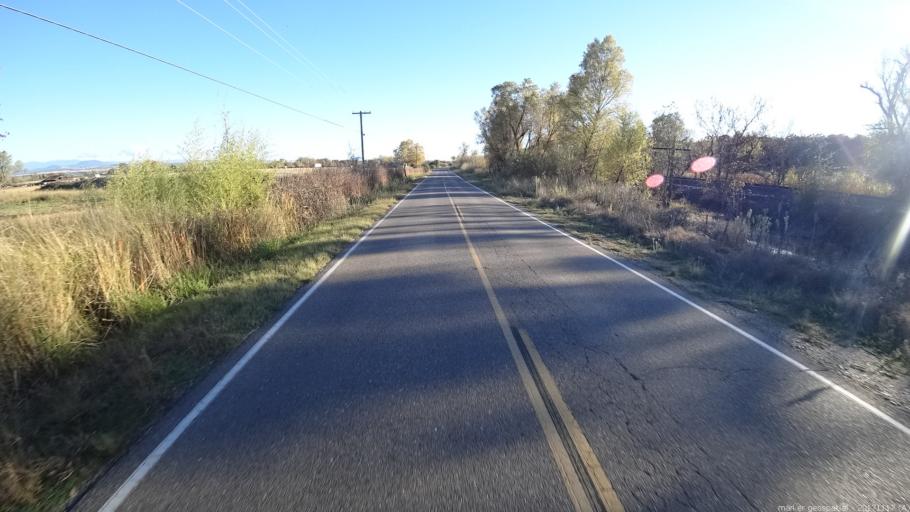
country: US
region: California
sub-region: Shasta County
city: Cottonwood
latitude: 40.4133
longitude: -122.2479
